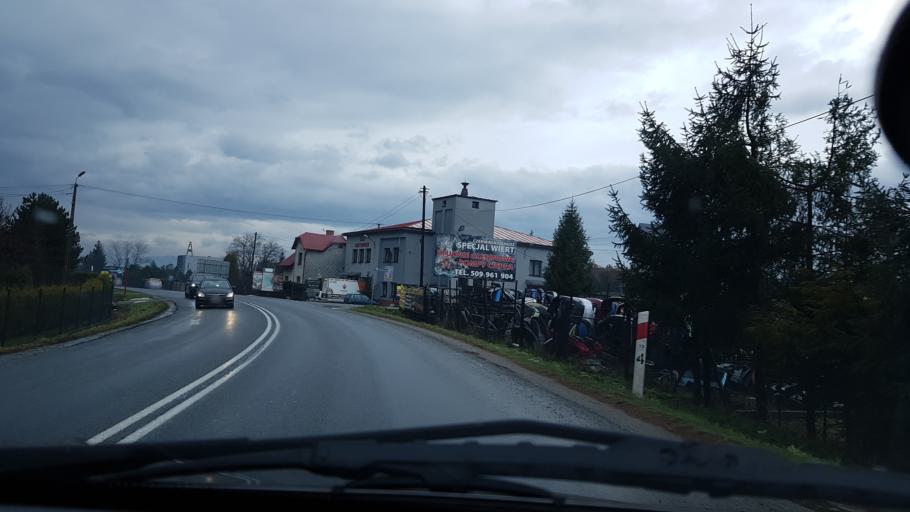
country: PL
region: Silesian Voivodeship
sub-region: Powiat zywiecki
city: Lodygowice
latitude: 49.7251
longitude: 19.1365
